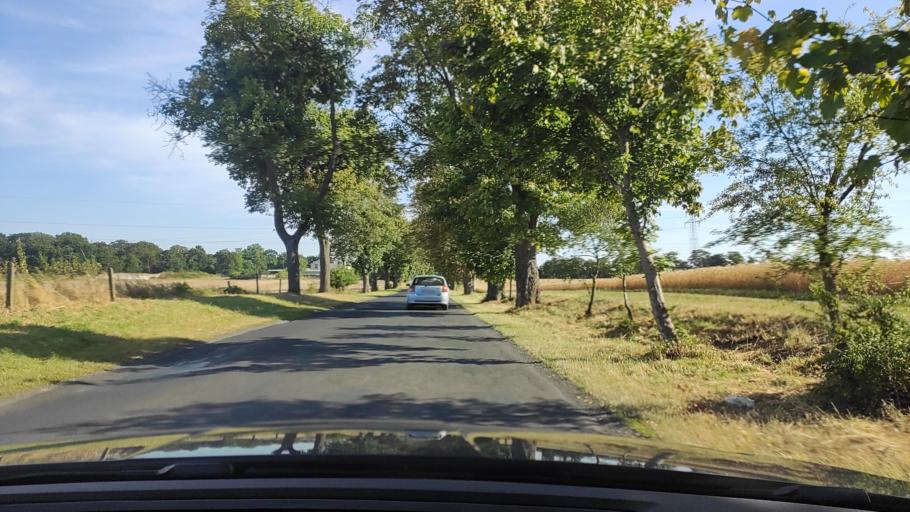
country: PL
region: Greater Poland Voivodeship
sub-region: Powiat poznanski
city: Kobylnica
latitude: 52.4839
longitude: 17.0940
